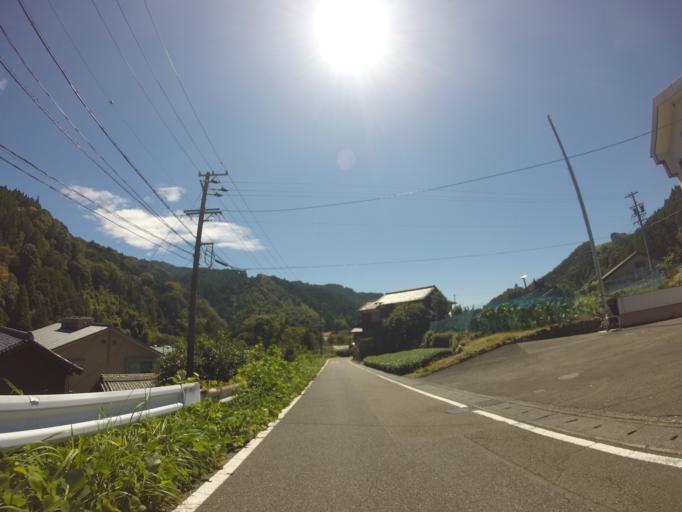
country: JP
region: Shizuoka
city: Fujieda
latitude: 34.9691
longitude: 138.2123
